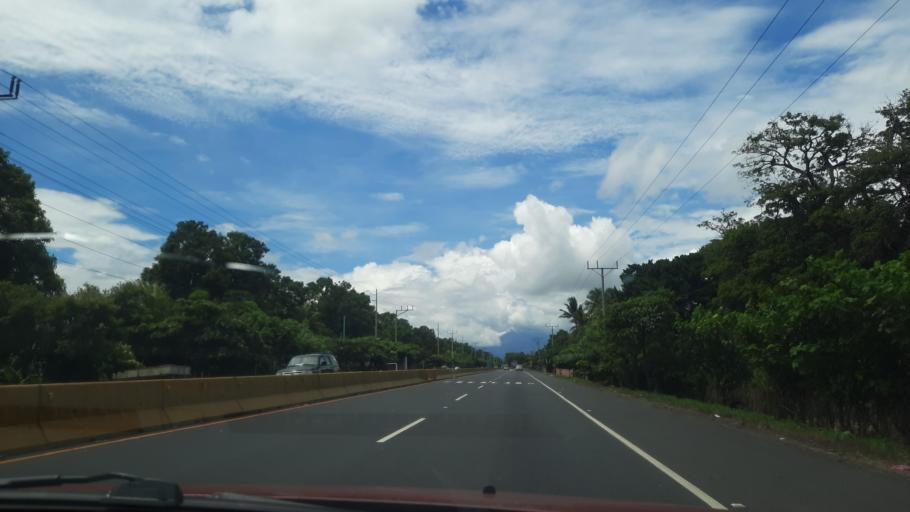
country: SV
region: Sonsonate
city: Acajutla
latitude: 13.6407
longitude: -89.7754
